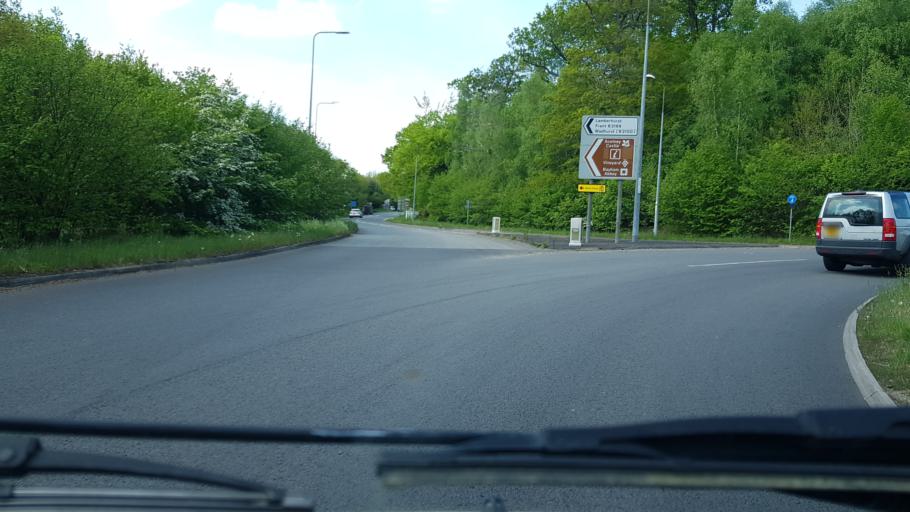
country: GB
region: England
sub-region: East Sussex
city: Wadhurst
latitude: 51.0911
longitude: 0.3955
